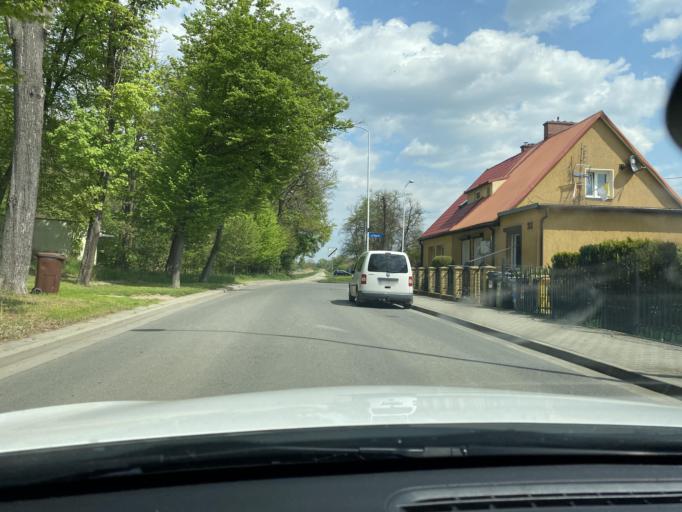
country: PL
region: Lower Silesian Voivodeship
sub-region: Powiat trzebnicki
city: Psary
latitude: 51.1522
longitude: 16.9938
